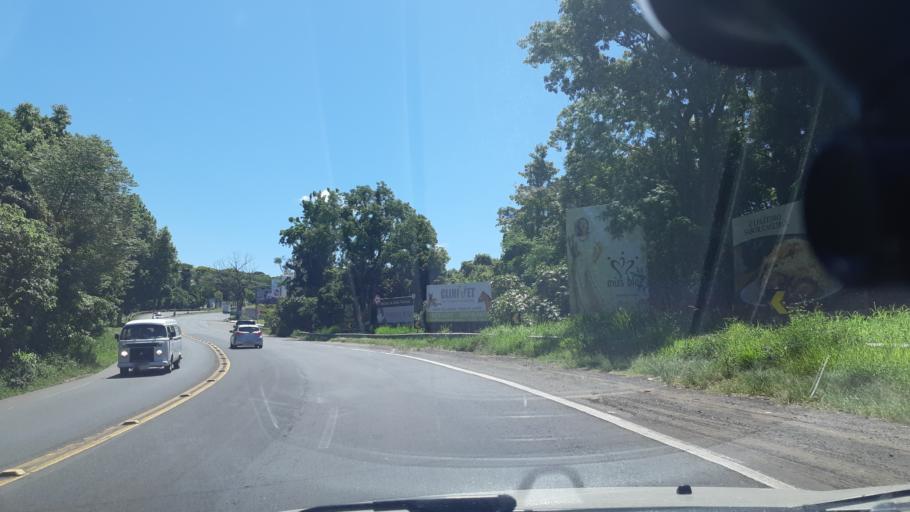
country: BR
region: Rio Grande do Sul
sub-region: Estancia Velha
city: Estancia Velha
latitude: -29.6282
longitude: -51.1393
